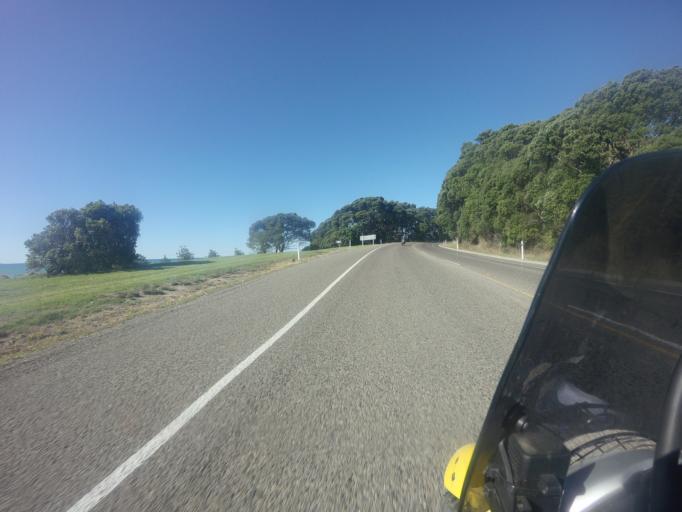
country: NZ
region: Bay of Plenty
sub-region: Opotiki District
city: Opotiki
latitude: -37.9918
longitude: 177.2188
